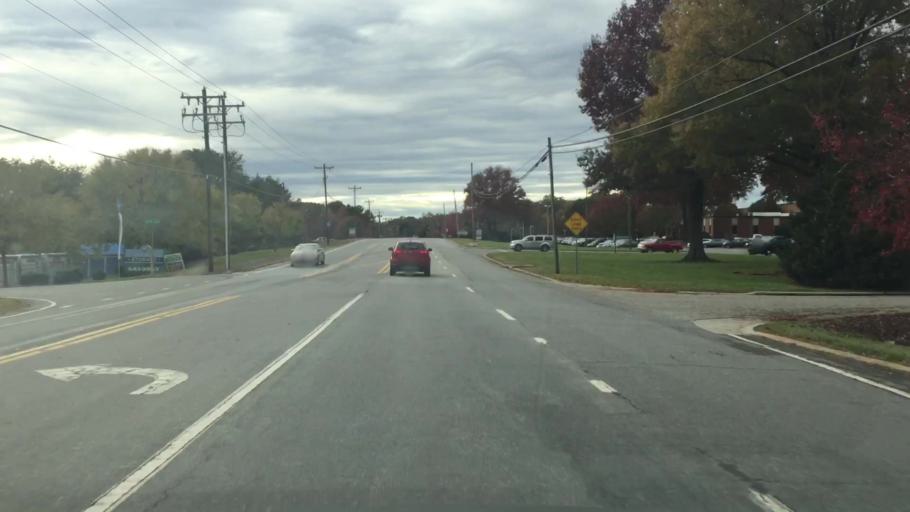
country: US
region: North Carolina
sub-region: Guilford County
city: Stokesdale
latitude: 36.2367
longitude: -79.9534
